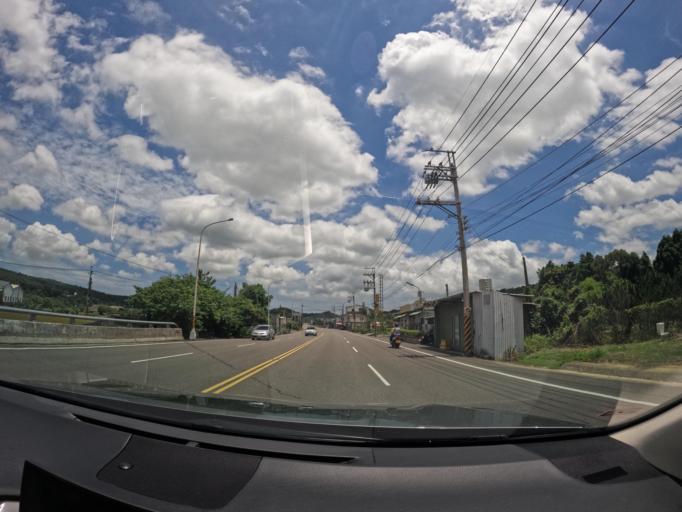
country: TW
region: Taiwan
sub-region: Miaoli
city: Miaoli
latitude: 24.6406
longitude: 120.9556
